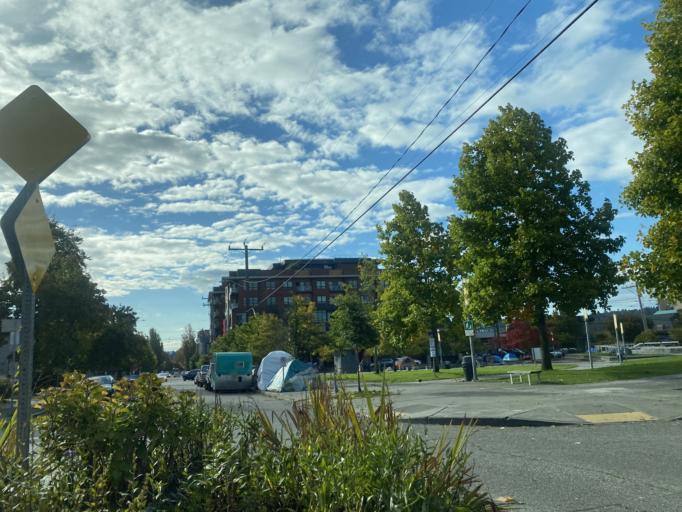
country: US
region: Washington
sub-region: King County
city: Seattle
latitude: 47.6710
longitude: -122.3847
